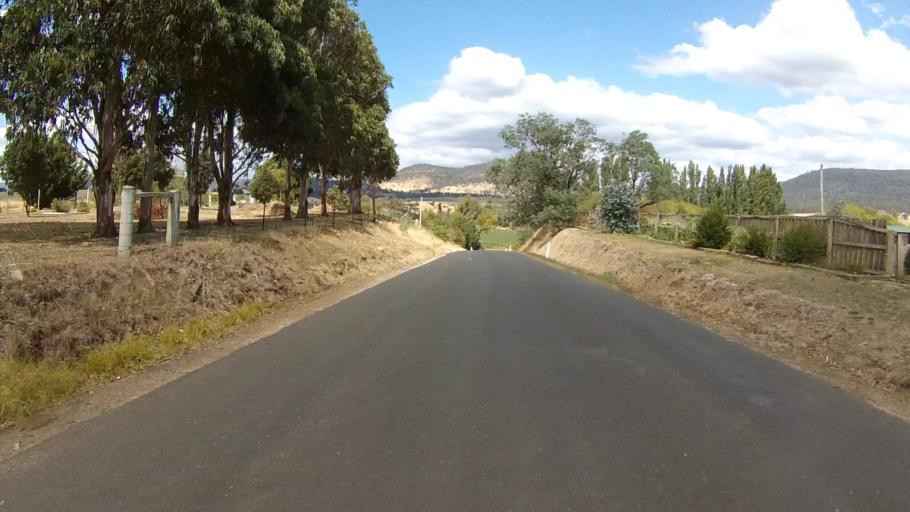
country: AU
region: Tasmania
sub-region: Derwent Valley
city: New Norfolk
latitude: -42.7512
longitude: 146.9723
